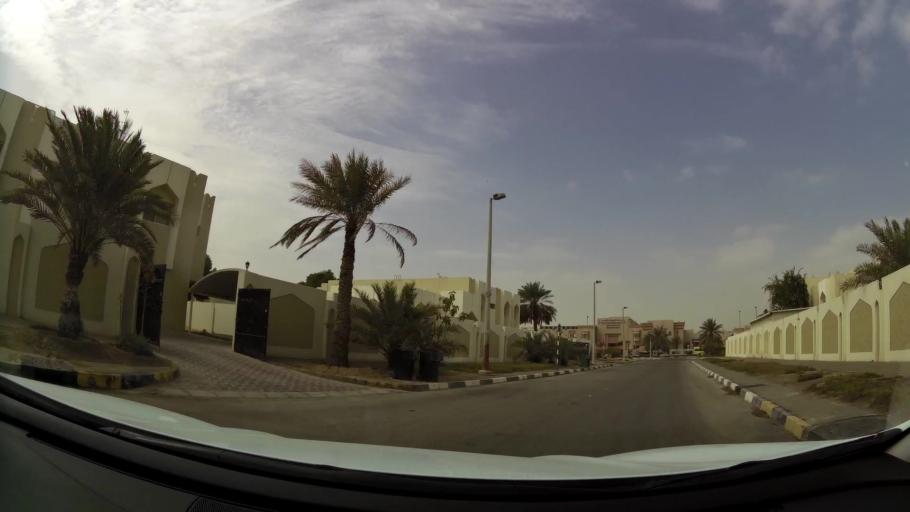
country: AE
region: Abu Dhabi
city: Abu Dhabi
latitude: 24.3953
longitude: 54.5023
